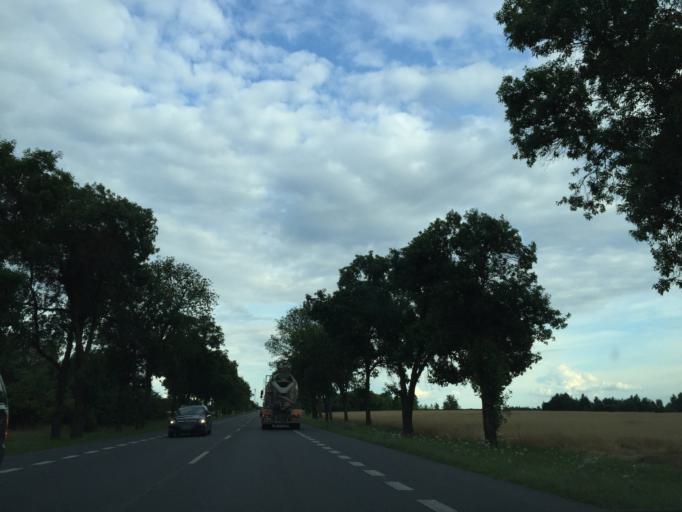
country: PL
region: Lublin Voivodeship
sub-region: Powiat lubartowski
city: Firlej
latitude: 51.5735
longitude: 22.4964
